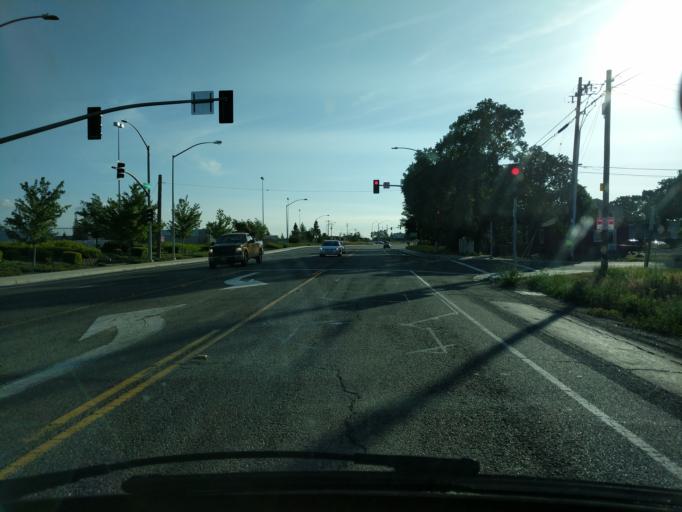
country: US
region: California
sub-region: San Joaquin County
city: Garden Acres
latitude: 37.9422
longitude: -121.2279
